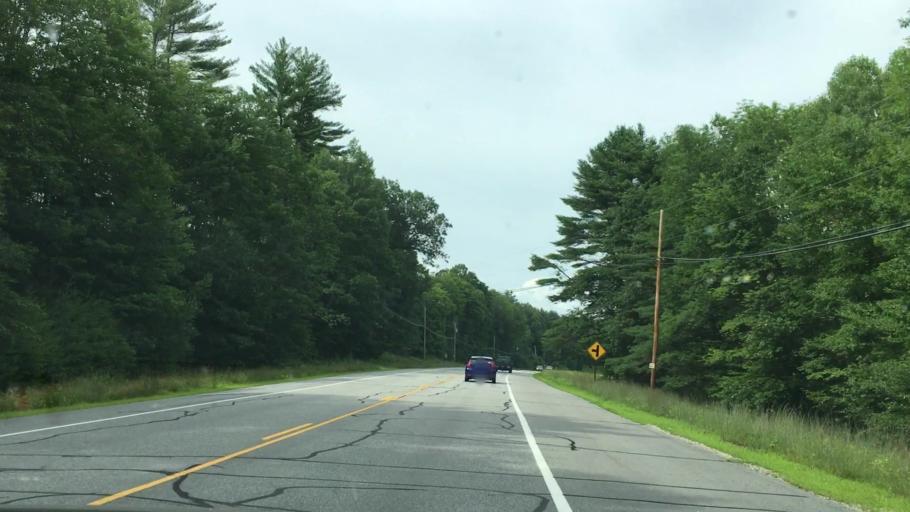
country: US
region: New Hampshire
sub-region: Hillsborough County
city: Hillsborough
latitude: 43.0900
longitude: -71.9197
